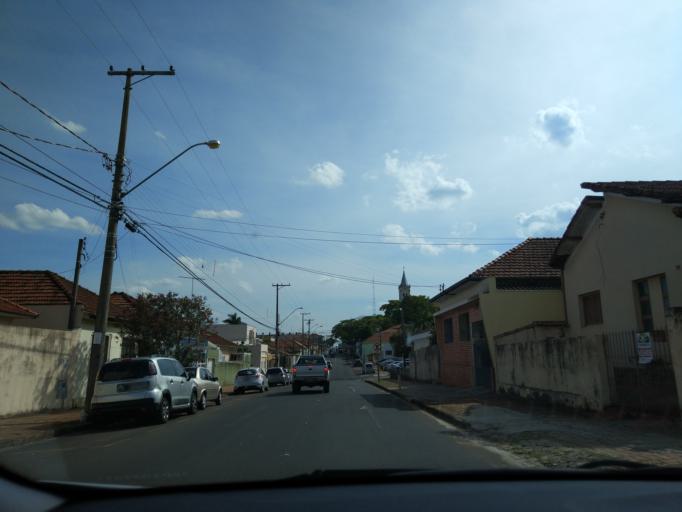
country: BR
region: Sao Paulo
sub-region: Botucatu
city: Botucatu
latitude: -22.8705
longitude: -48.4452
